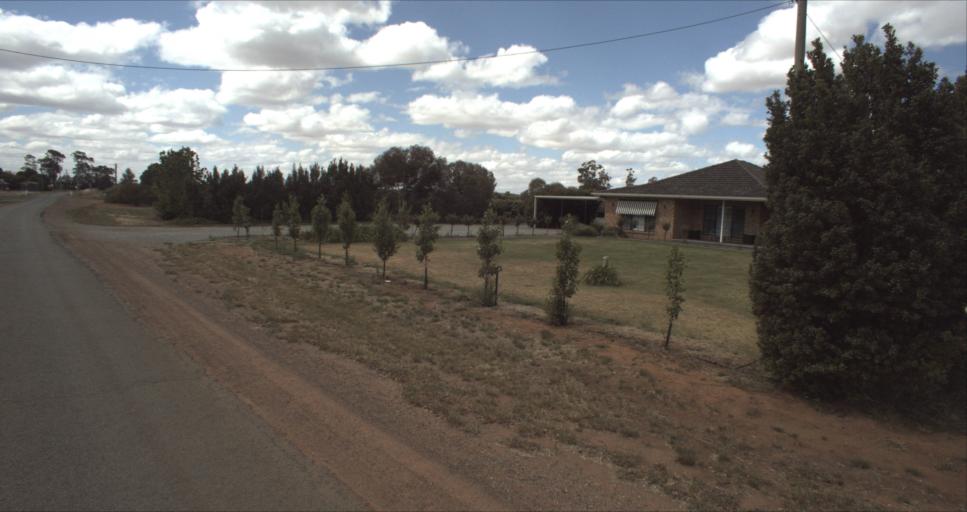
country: AU
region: New South Wales
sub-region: Leeton
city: Leeton
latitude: -34.5819
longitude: 146.3968
